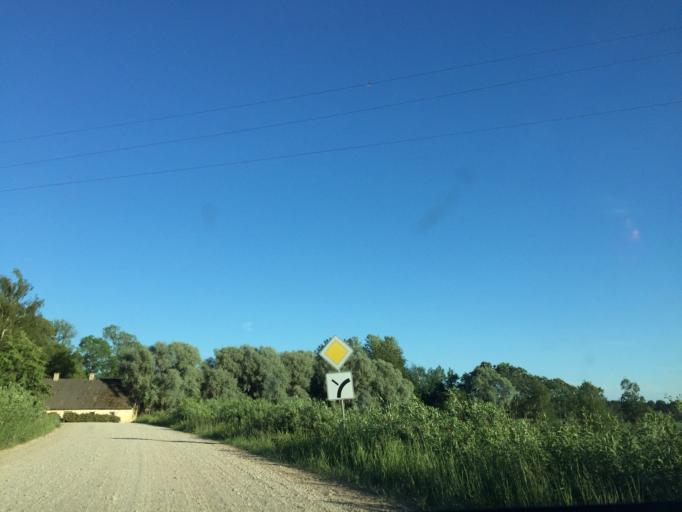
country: LV
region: Broceni
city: Broceni
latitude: 56.7859
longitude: 22.5619
